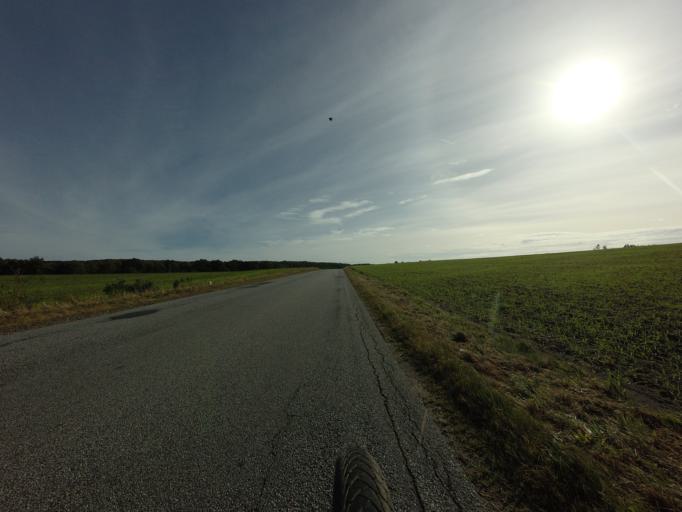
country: DK
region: Central Jutland
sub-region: Viborg Kommune
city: Viborg
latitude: 56.4324
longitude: 9.4262
